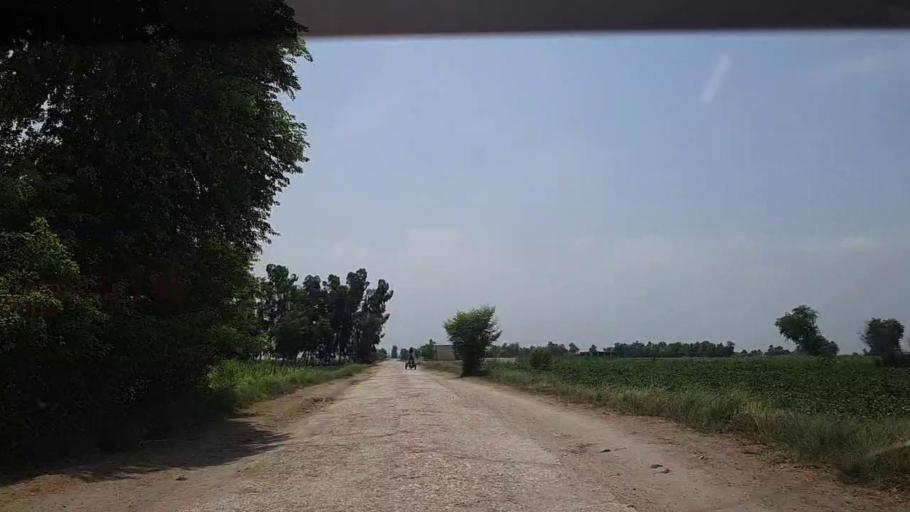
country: PK
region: Sindh
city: Khanpur
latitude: 27.9129
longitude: 69.3952
